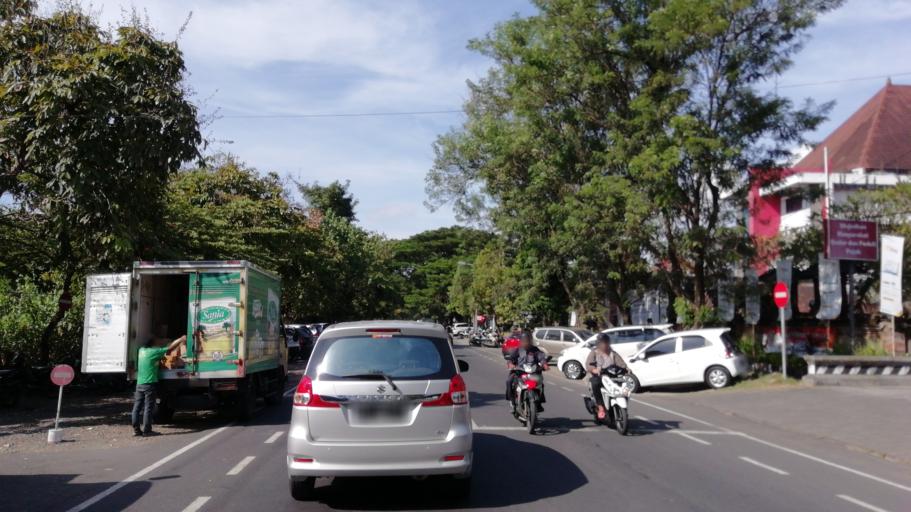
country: ID
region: Bali
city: Denpasar
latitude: -8.6678
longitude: 115.2284
